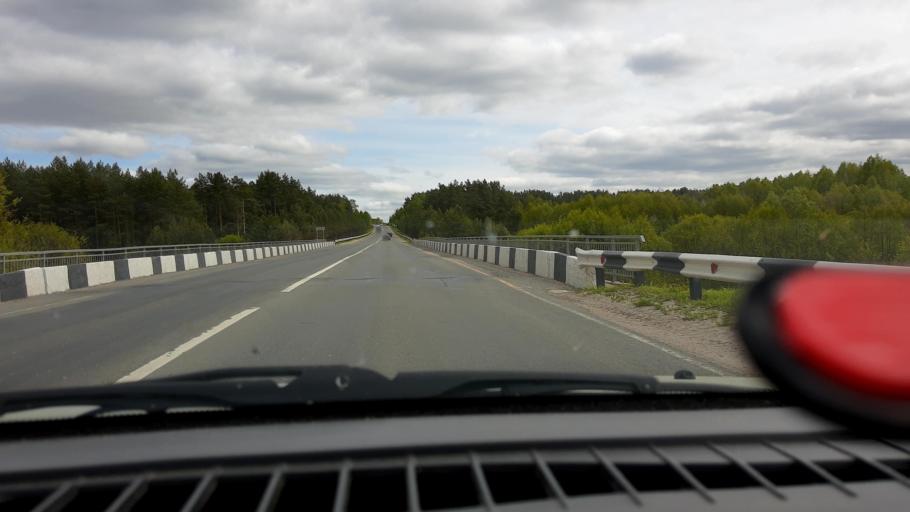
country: RU
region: Nizjnij Novgorod
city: Sitniki
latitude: 56.4775
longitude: 44.0272
